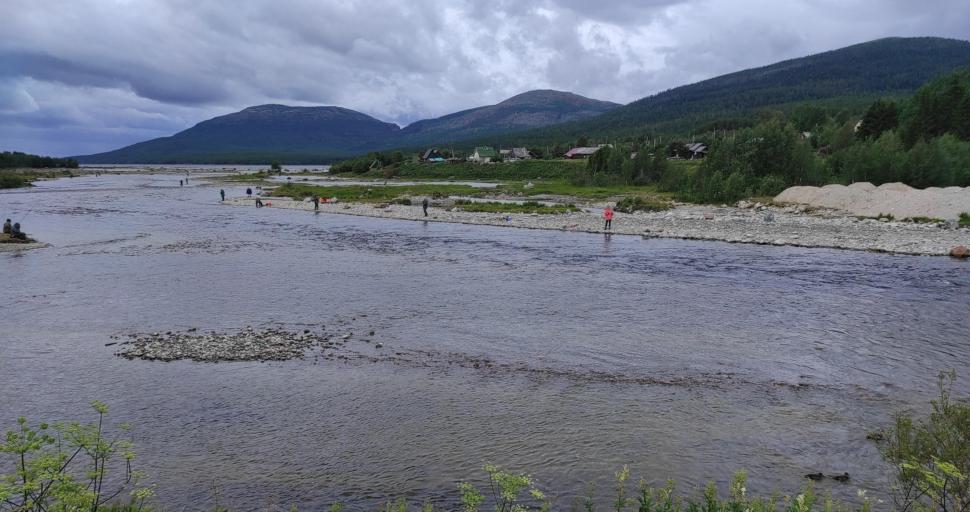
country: RU
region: Murmansk
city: Afrikanda
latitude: 67.0832
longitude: 32.9966
